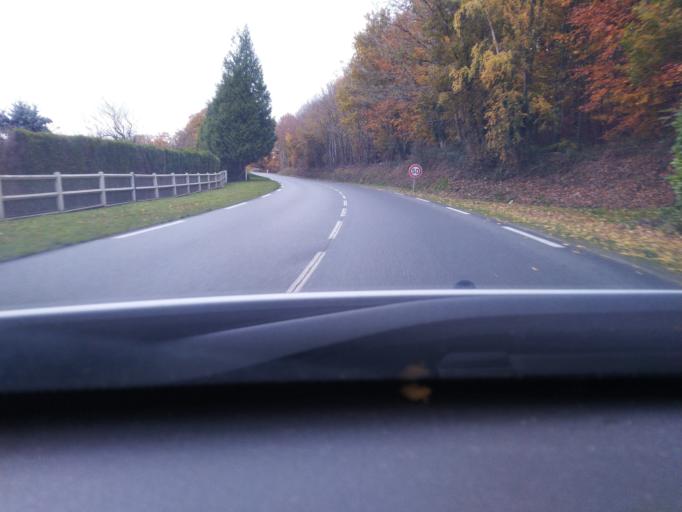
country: FR
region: Haute-Normandie
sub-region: Departement de la Seine-Maritime
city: Duclair
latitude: 49.4875
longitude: 0.8882
